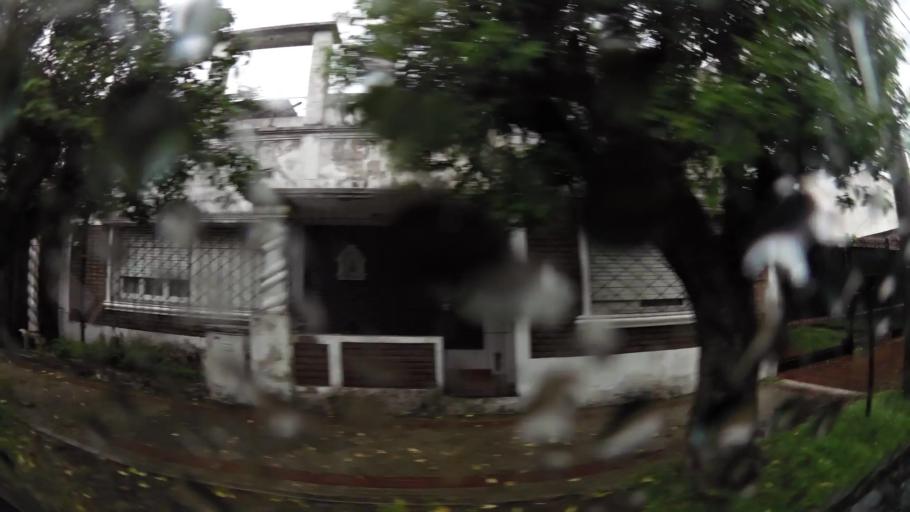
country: AR
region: Buenos Aires
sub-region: Partido de Lanus
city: Lanus
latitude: -34.7243
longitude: -58.4046
